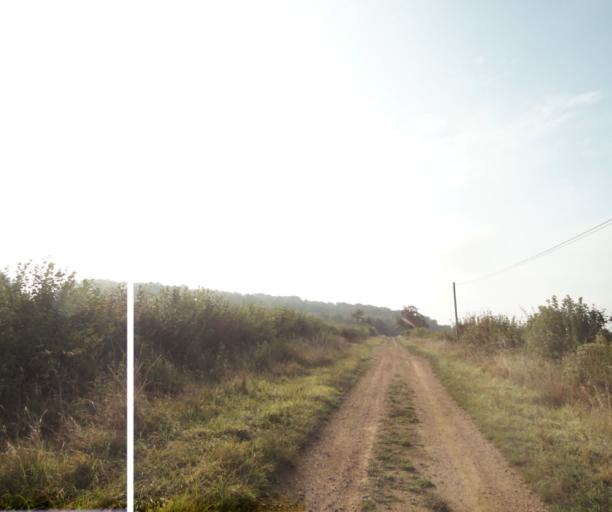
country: FR
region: Bourgogne
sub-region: Departement de Saone-et-Loire
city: Charolles
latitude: 46.4782
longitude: 4.2750
